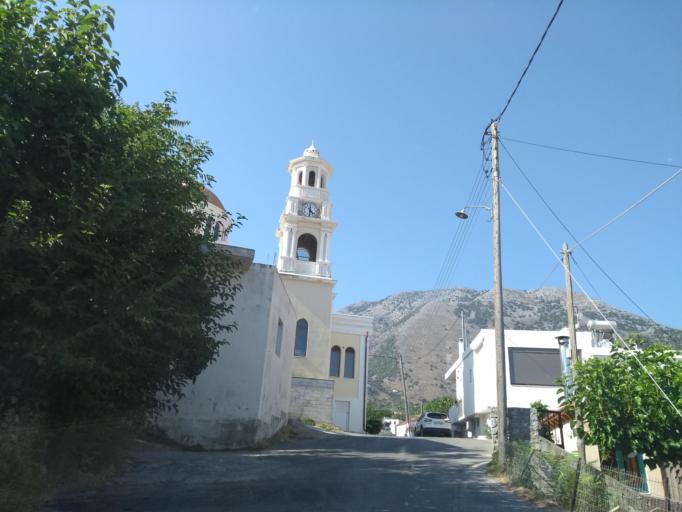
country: GR
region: Crete
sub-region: Nomos Chanias
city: Georgioupolis
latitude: 35.3154
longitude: 24.2957
